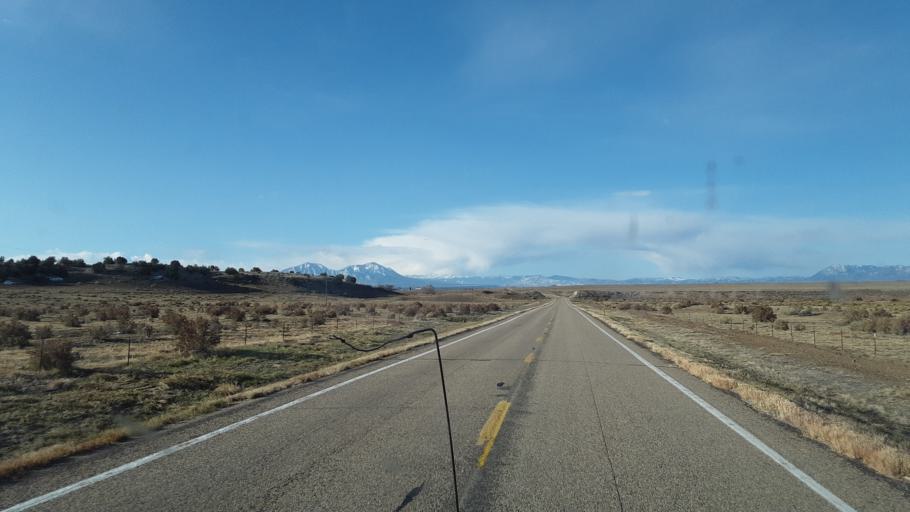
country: US
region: Colorado
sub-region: Huerfano County
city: Walsenburg
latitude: 37.6847
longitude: -104.6457
